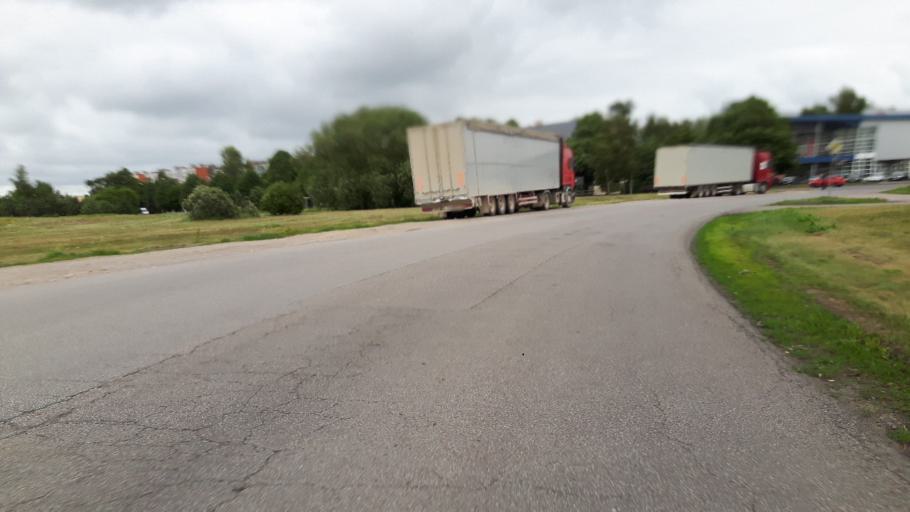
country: LV
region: Liepaja
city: Vec-Liepaja
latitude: 56.5364
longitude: 21.0006
